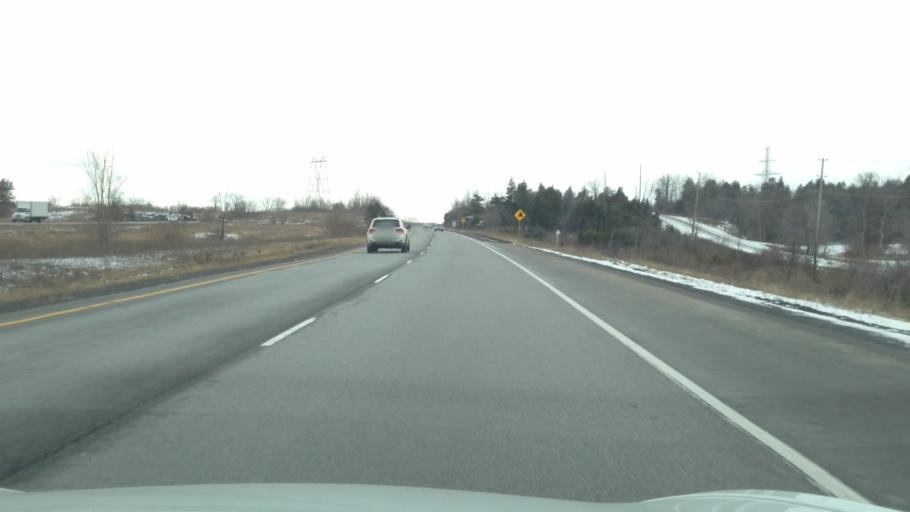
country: CA
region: Ontario
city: Casselman
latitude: 45.3764
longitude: -74.8412
